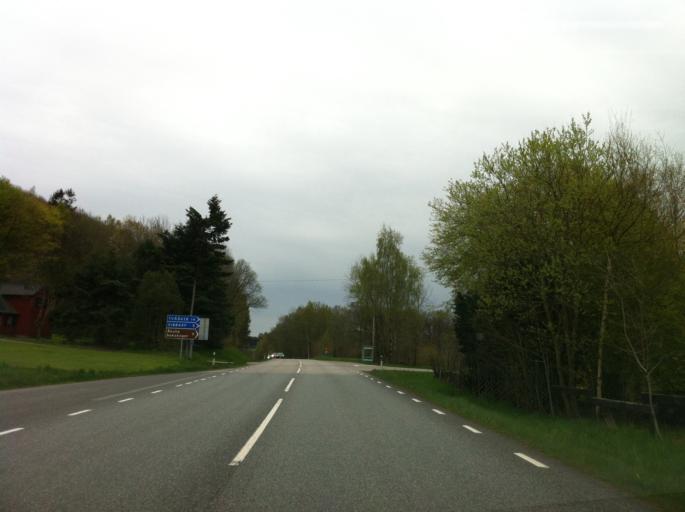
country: SE
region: Halland
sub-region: Falkenbergs Kommun
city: Falkenberg
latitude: 57.0290
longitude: 12.5968
